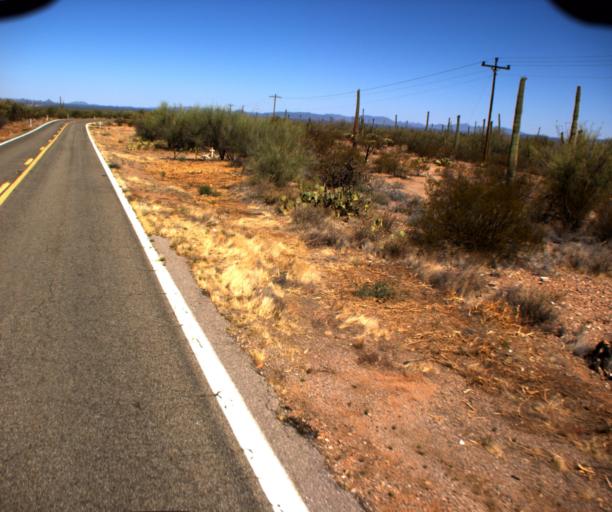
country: US
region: Arizona
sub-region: Pima County
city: Sells
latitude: 32.1777
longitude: -112.2705
